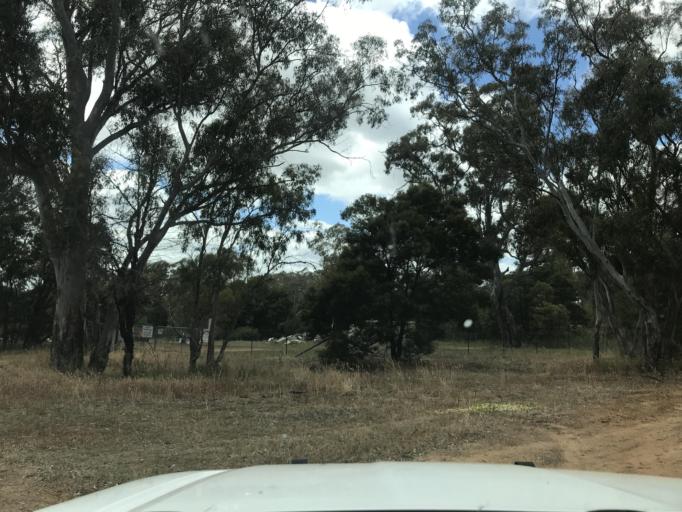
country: AU
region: South Australia
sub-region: Wattle Range
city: Penola
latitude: -37.3690
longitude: 141.2180
